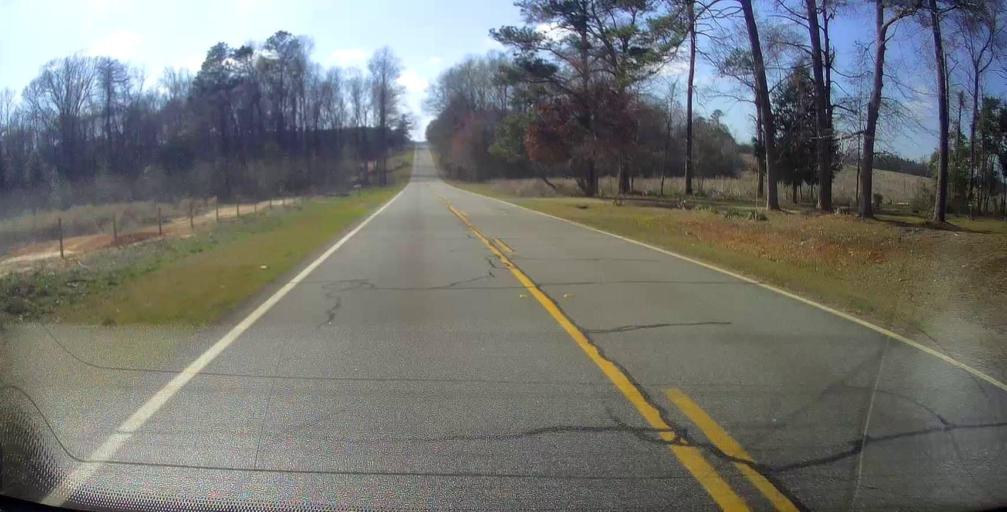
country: US
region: Georgia
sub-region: Twiggs County
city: Jeffersonville
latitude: 32.6811
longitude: -83.2981
